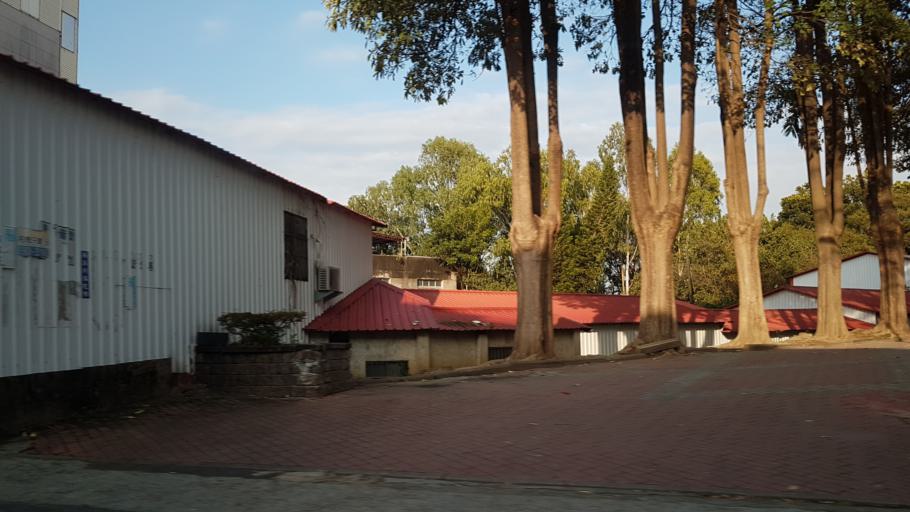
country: TW
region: Taiwan
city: Xinying
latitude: 23.3464
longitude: 120.4163
